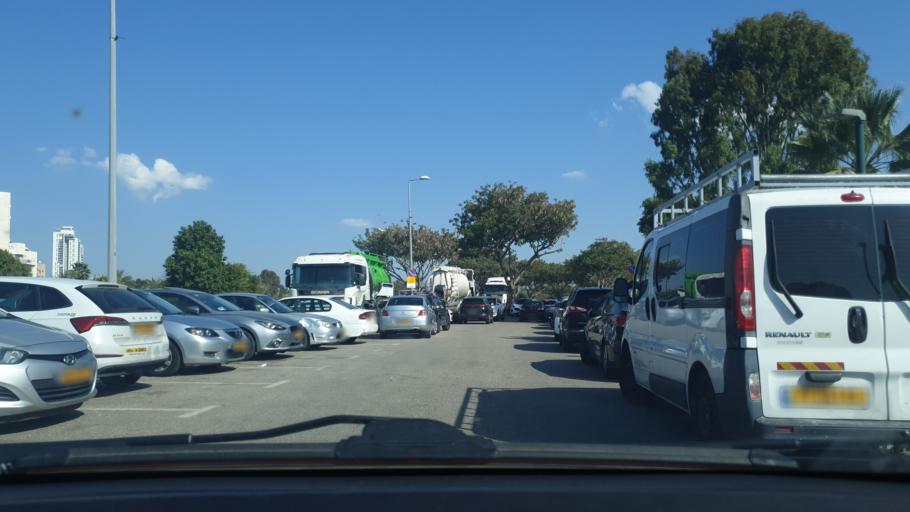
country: IL
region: Tel Aviv
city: Azor
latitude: 32.0435
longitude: 34.8063
